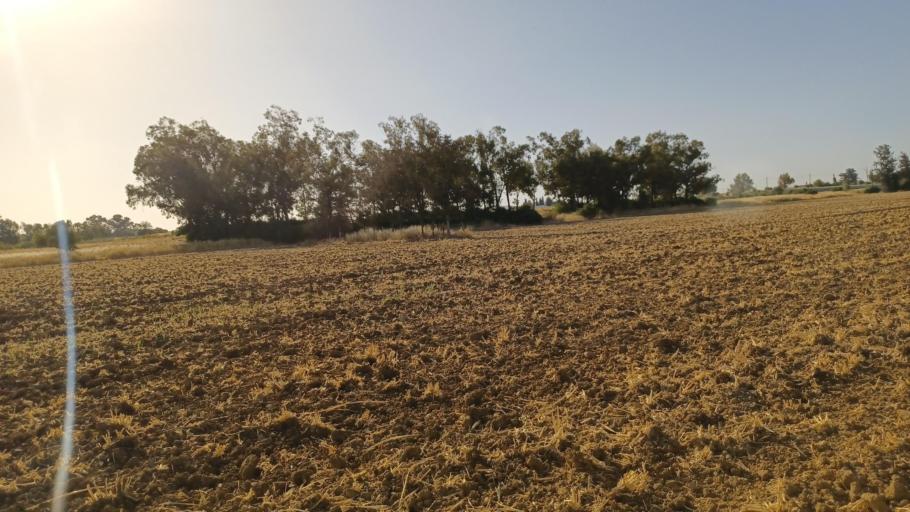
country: CY
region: Lefkosia
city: Mammari
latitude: 35.1699
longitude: 33.2469
